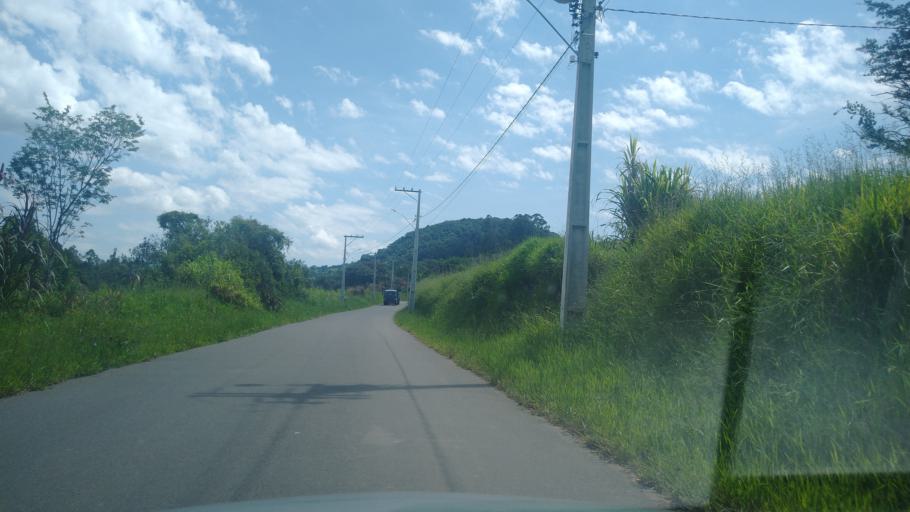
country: BR
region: Minas Gerais
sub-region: Extrema
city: Extrema
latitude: -22.7959
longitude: -46.2903
